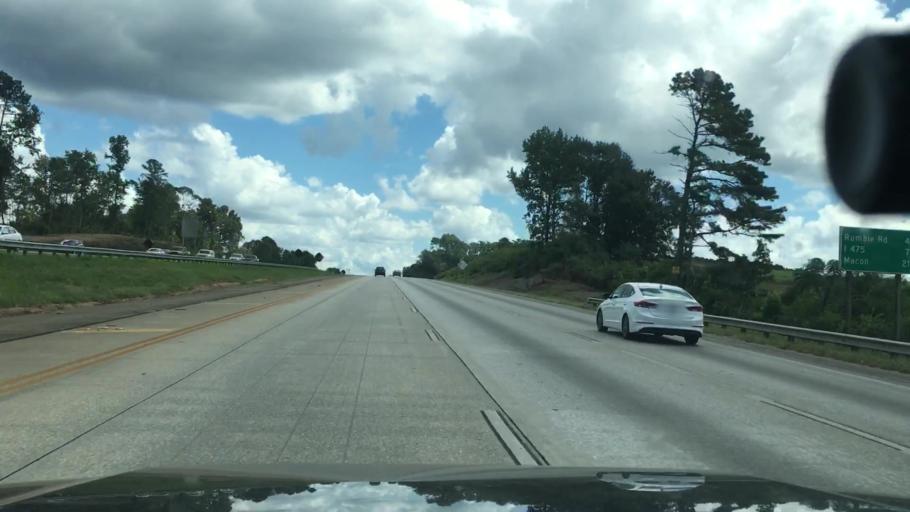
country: US
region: Georgia
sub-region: Monroe County
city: Forsyth
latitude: 33.0210
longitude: -83.8969
